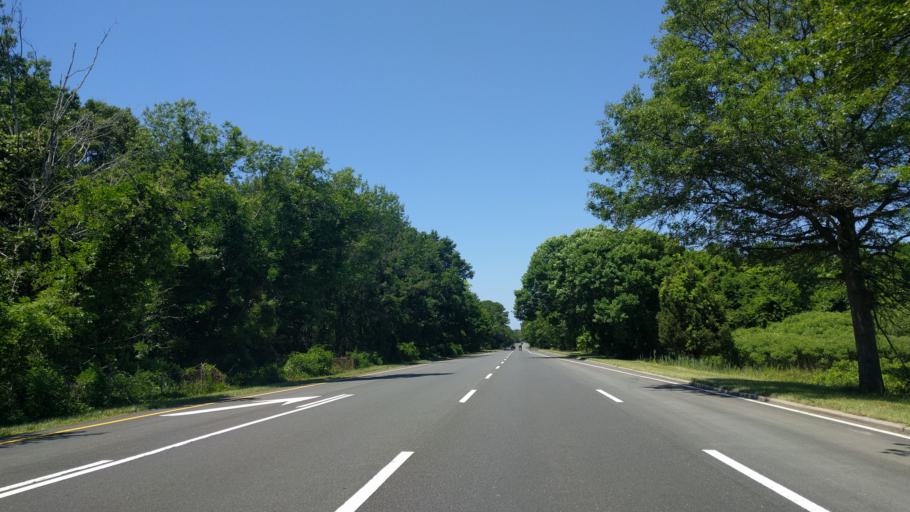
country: US
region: New York
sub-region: Suffolk County
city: Manorville
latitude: 40.8619
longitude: -72.7690
